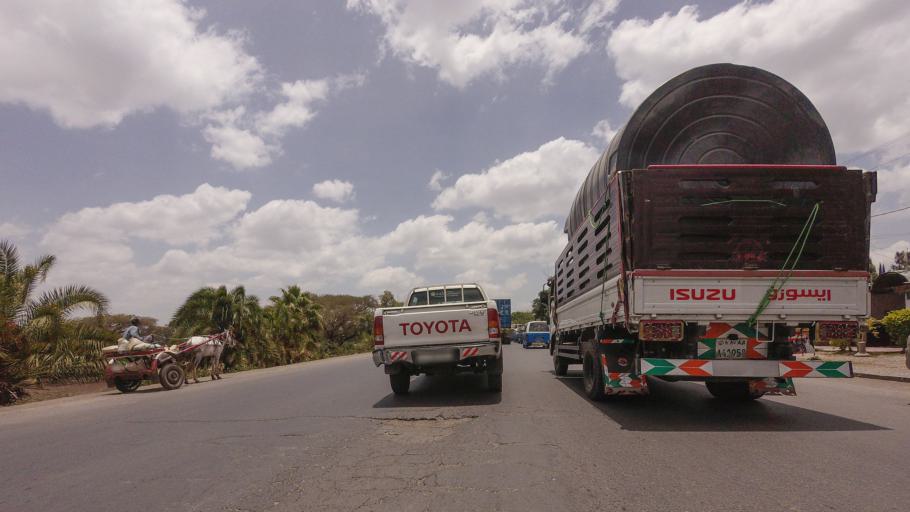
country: ET
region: Oromiya
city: Bishoftu
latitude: 8.7514
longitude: 38.9624
